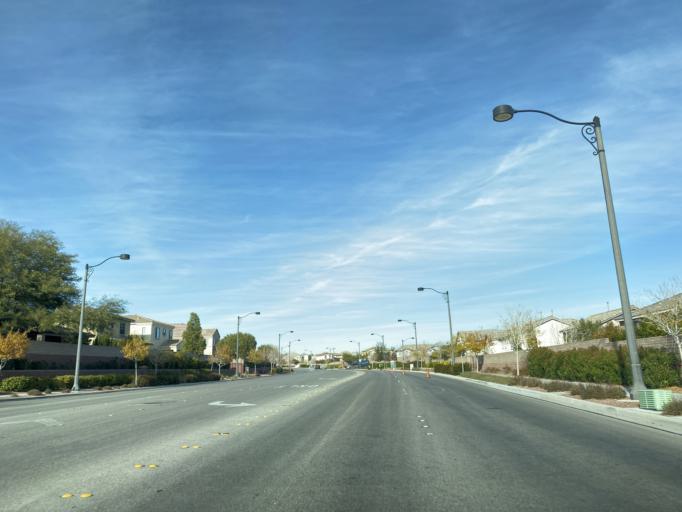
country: US
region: Nevada
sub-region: Clark County
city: Summerlin South
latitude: 36.2998
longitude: -115.3195
